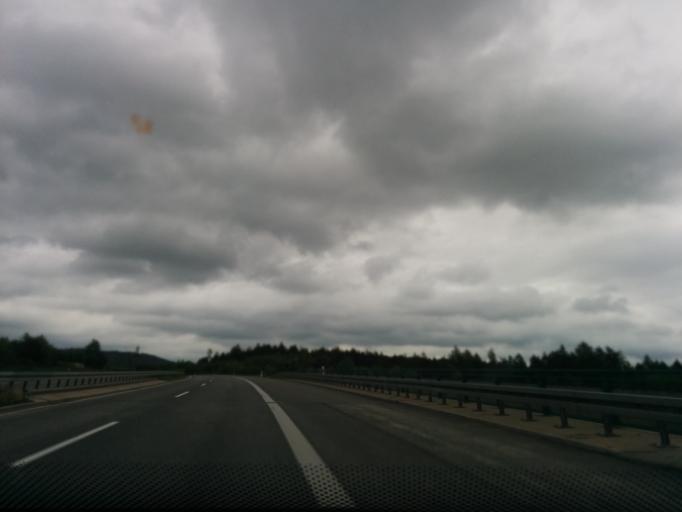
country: DE
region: Thuringia
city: Suhl
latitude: 50.6086
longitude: 10.6448
